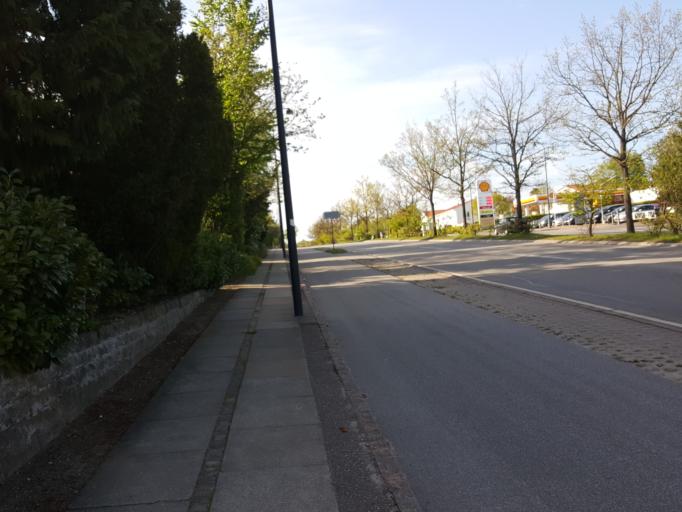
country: DK
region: Capital Region
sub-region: Rudersdal Kommune
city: Holte
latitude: 55.8176
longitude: 12.4682
